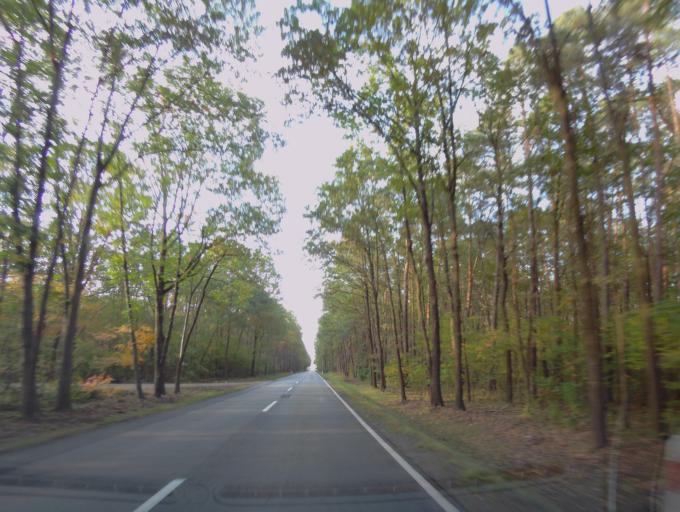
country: PL
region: Subcarpathian Voivodeship
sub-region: Powiat nizanski
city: Krzeszow
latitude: 50.3932
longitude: 22.3011
